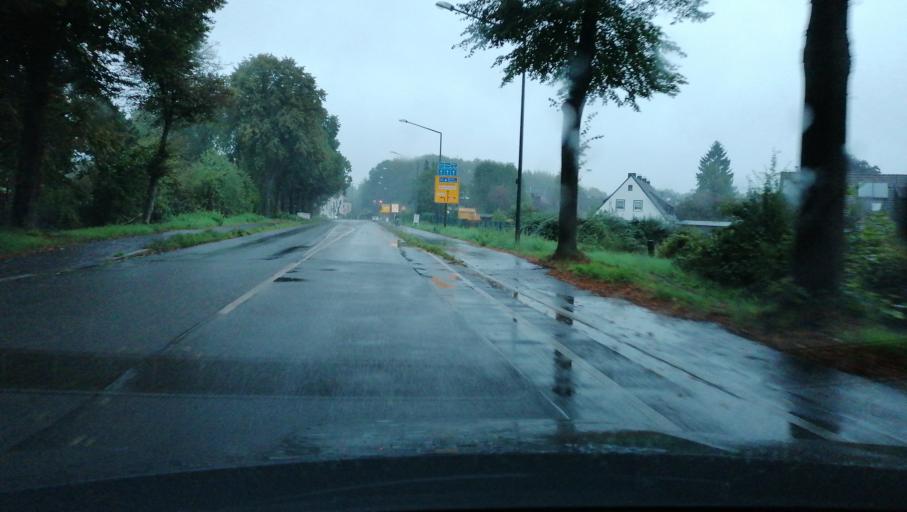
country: DE
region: North Rhine-Westphalia
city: Herten
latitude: 51.5791
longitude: 7.1558
